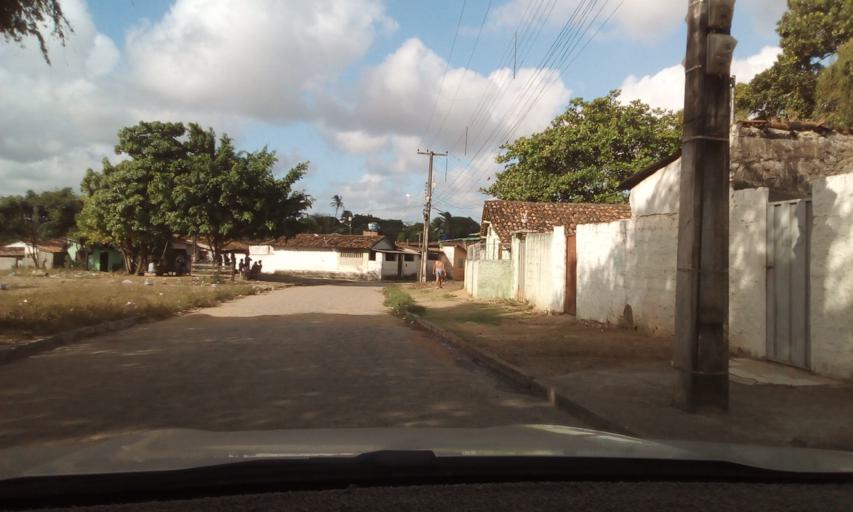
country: BR
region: Paraiba
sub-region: Bayeux
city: Bayeux
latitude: -7.1529
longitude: -34.9074
